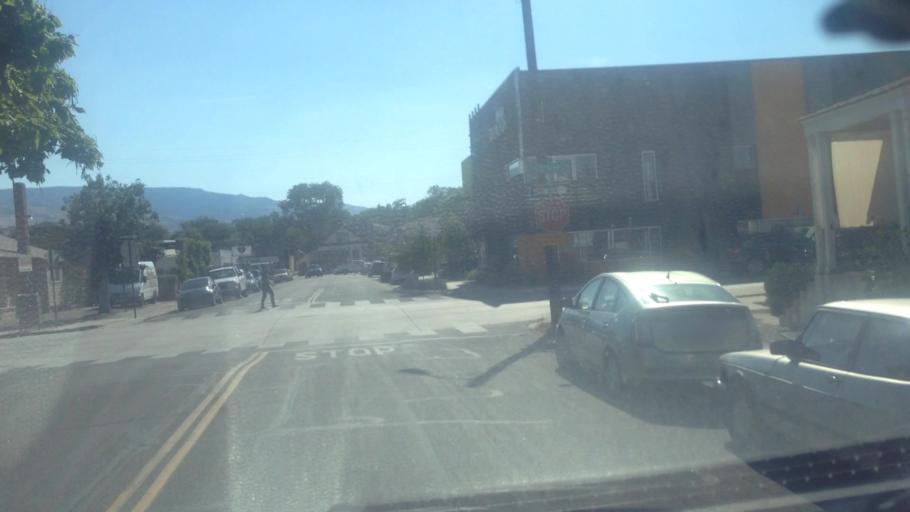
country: US
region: Nevada
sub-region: Washoe County
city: Reno
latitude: 39.5182
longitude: -119.8075
